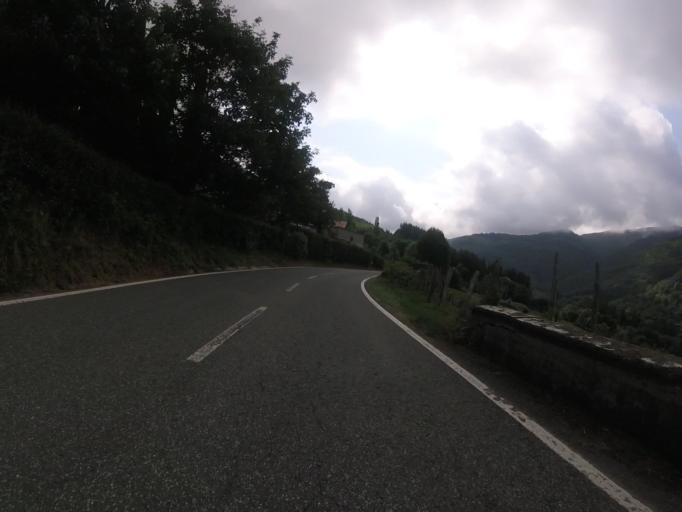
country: ES
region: Navarre
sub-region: Provincia de Navarra
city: Ezkurra
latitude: 43.0846
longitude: -1.8236
